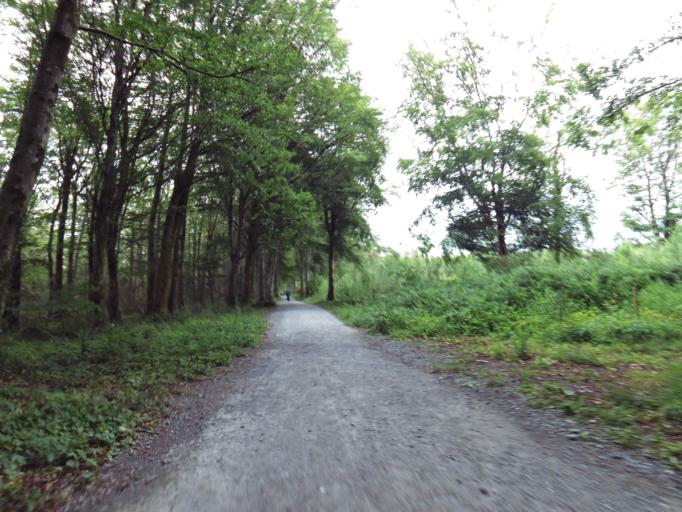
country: IE
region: Connaught
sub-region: County Galway
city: Gort
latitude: 53.0879
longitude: -8.8453
